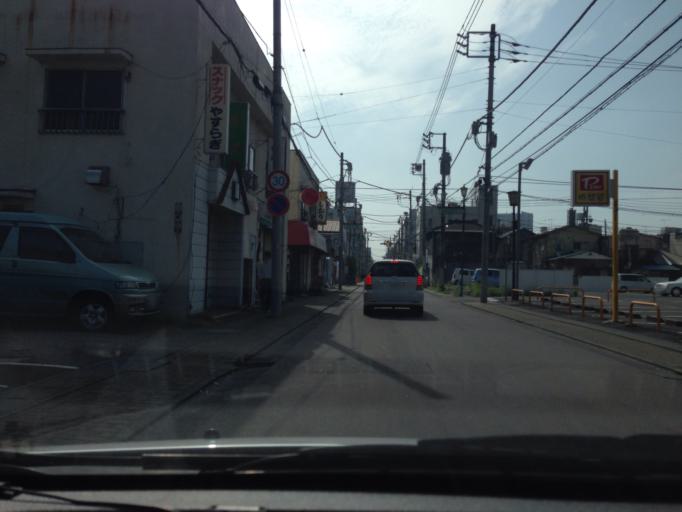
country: JP
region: Ibaraki
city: Naka
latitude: 36.0782
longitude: 140.1985
